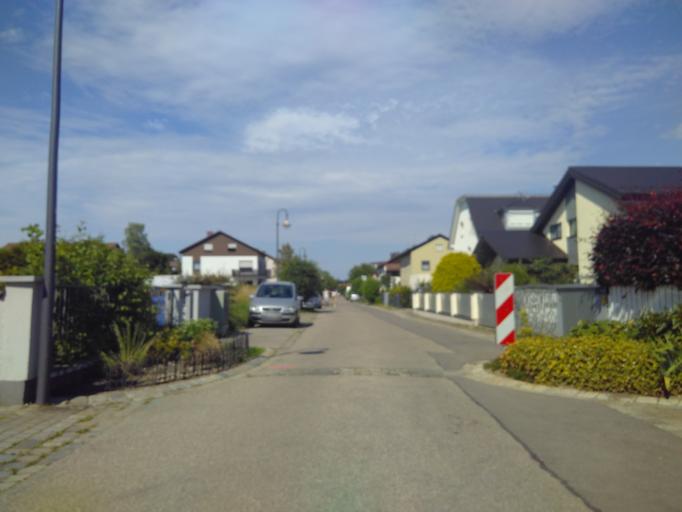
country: DE
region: Bavaria
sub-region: Upper Bavaria
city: Olching
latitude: 48.2056
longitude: 11.3330
